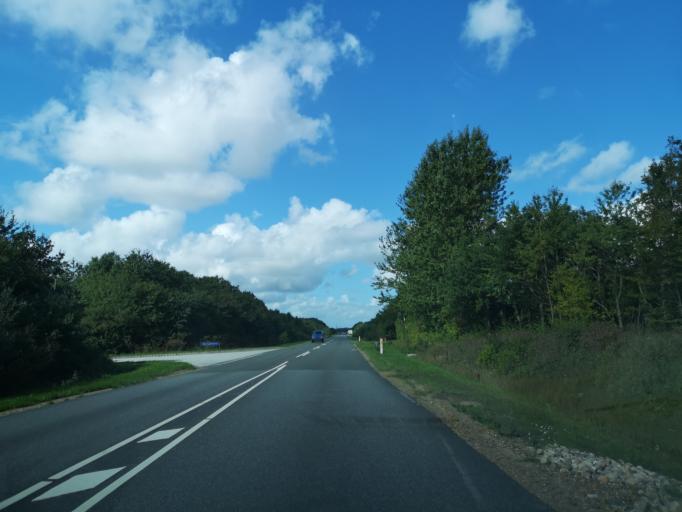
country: DK
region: Central Jutland
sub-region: Holstebro Kommune
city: Holstebro
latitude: 56.3883
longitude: 8.6069
